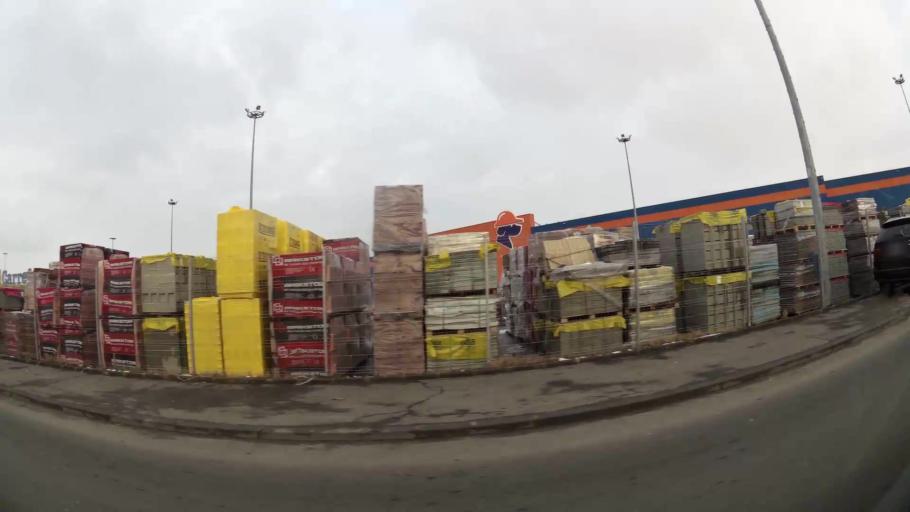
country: RO
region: Ilfov
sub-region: Comuna Fundeni-Dobroesti
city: Fundeni
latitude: 44.4733
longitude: 26.1612
